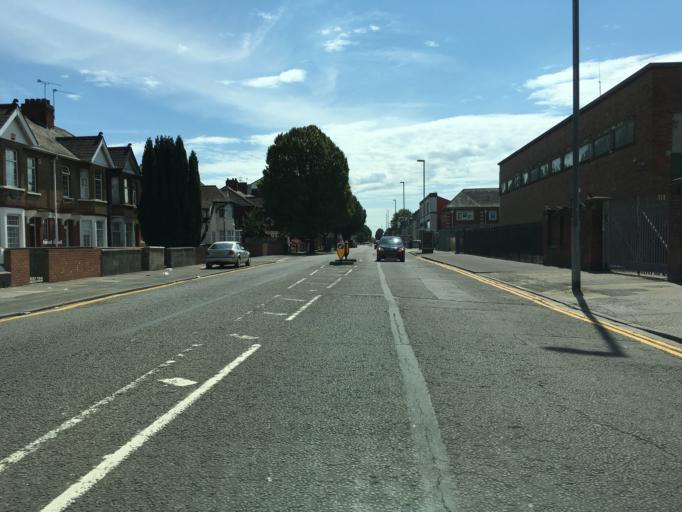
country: GB
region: Wales
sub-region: Newport
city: Newport
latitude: 51.5875
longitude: -2.9845
